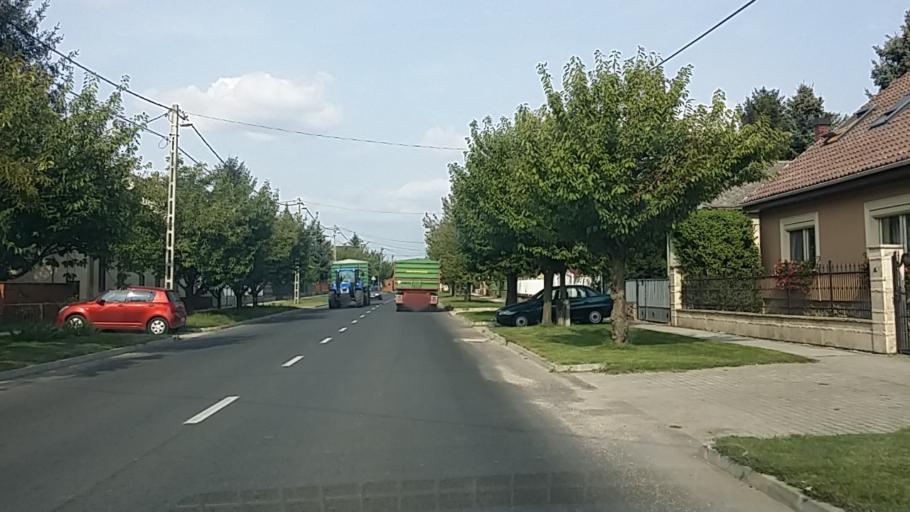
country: HU
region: Gyor-Moson-Sopron
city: Bony
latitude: 47.6498
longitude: 17.9185
